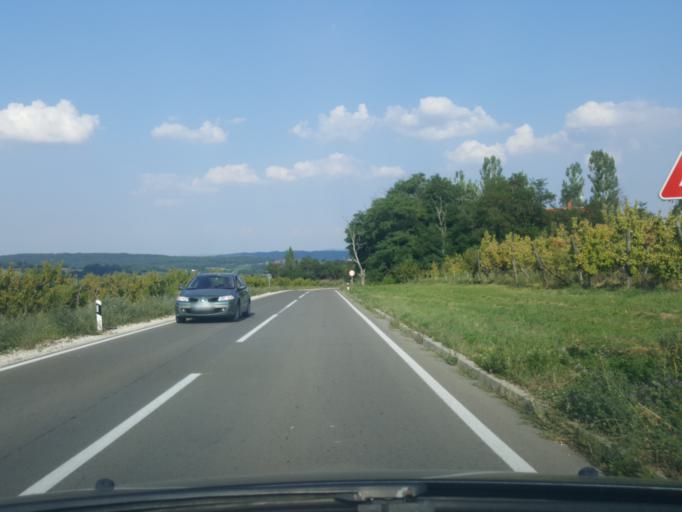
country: RS
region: Central Serbia
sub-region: Sumadijski Okrug
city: Topola
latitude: 44.2278
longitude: 20.6446
